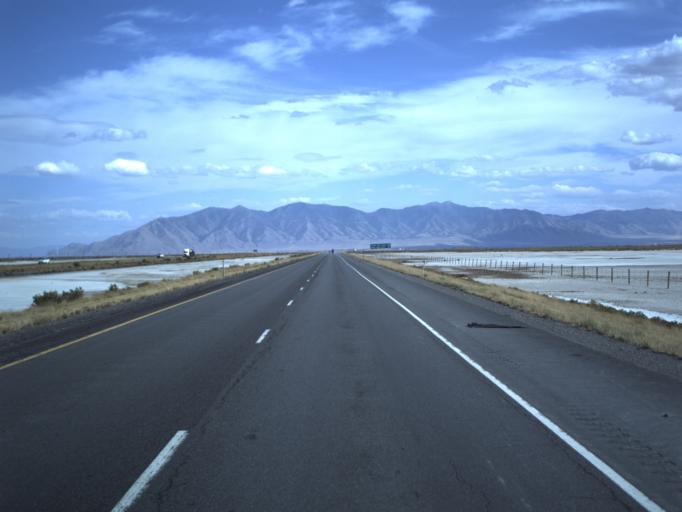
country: US
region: Utah
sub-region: Tooele County
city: Grantsville
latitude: 40.7045
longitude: -112.5114
